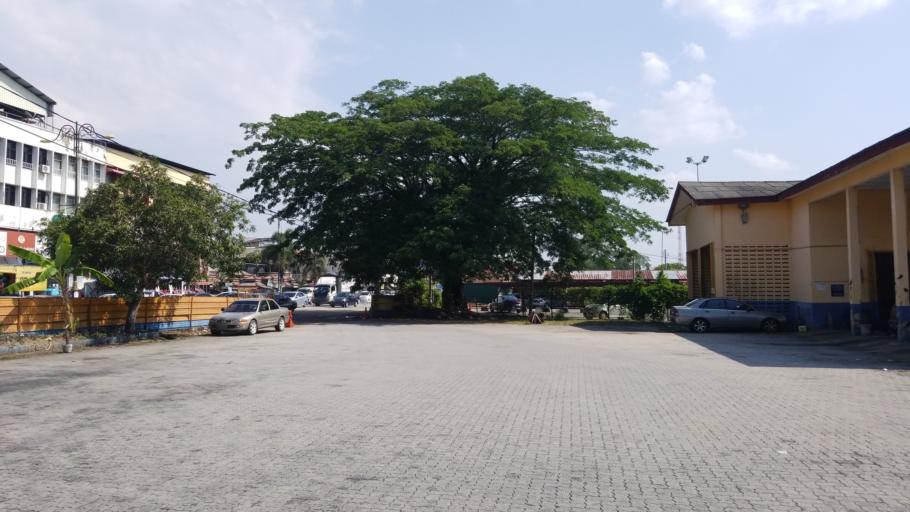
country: MY
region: Kelantan
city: Pasir Mas
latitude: 6.0440
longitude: 102.1437
